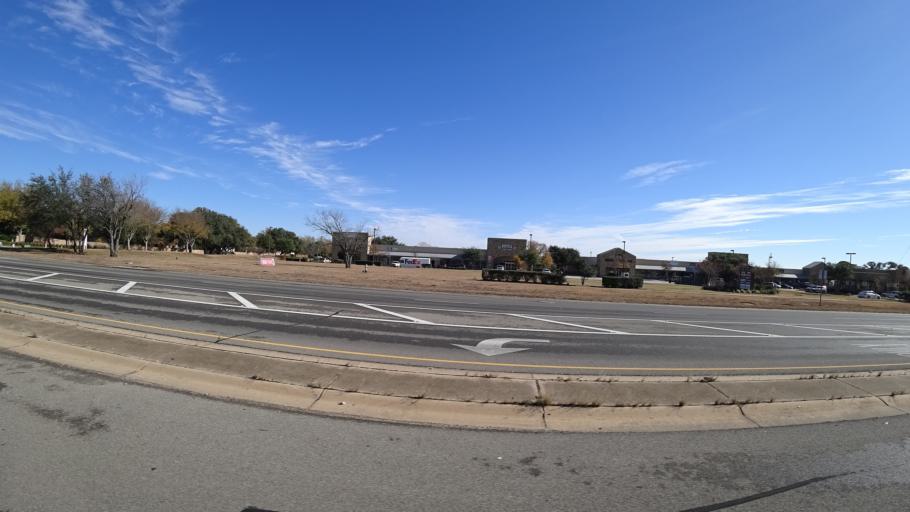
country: US
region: Texas
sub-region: Williamson County
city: Brushy Creek
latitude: 30.4875
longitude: -97.7712
